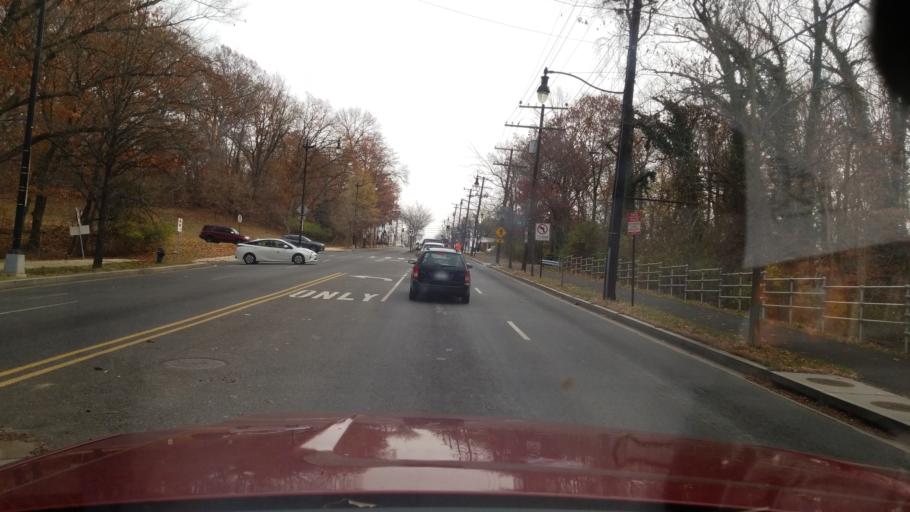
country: US
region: Maryland
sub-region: Prince George's County
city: Silver Hill
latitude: 38.8665
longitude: -76.9535
